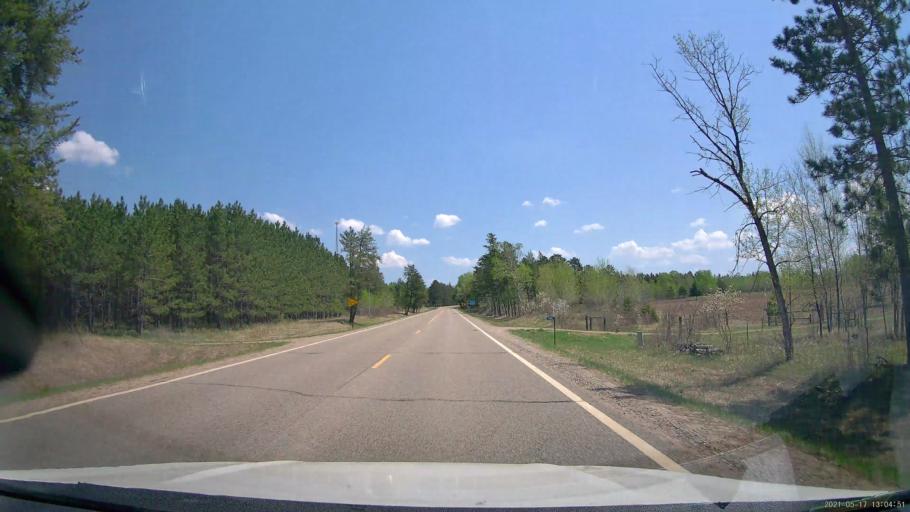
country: US
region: Minnesota
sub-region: Hubbard County
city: Park Rapids
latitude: 47.0651
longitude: -94.9532
